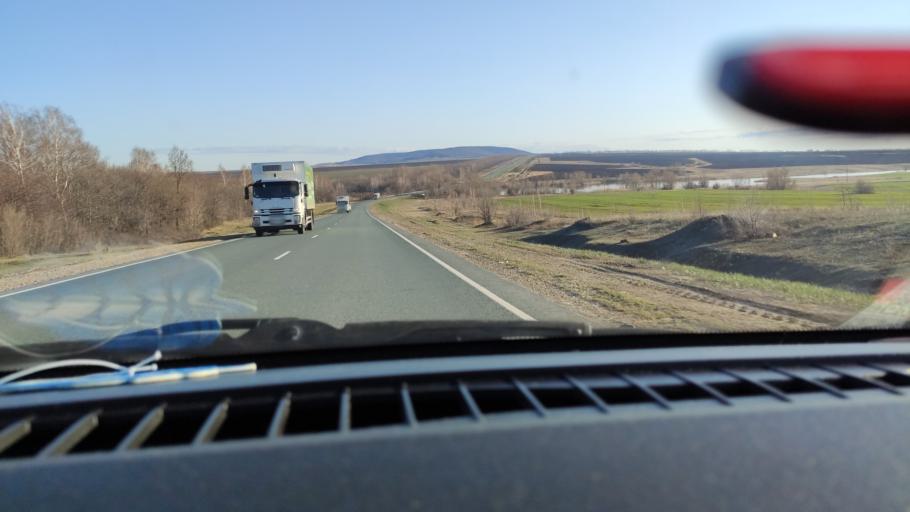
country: RU
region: Saratov
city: Alekseyevka
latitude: 52.2422
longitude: 47.9065
